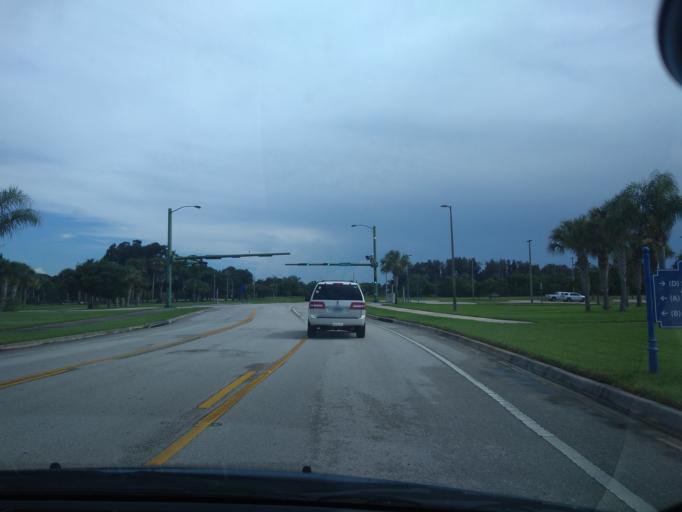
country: US
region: Florida
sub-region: Indian River County
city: West Vero Corridor
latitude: 27.6341
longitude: -80.4552
